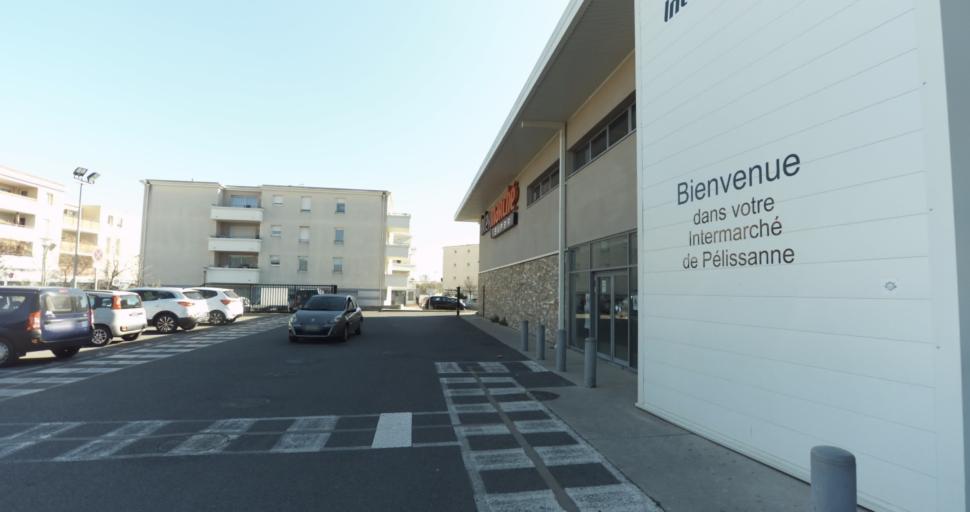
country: FR
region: Provence-Alpes-Cote d'Azur
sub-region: Departement des Bouches-du-Rhone
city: Pelissanne
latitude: 43.6324
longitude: 5.1391
